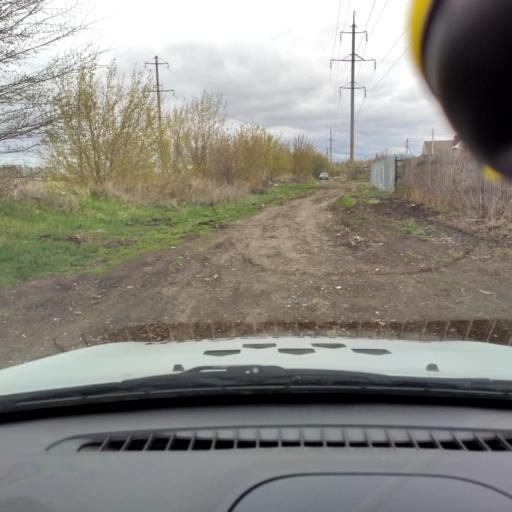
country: RU
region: Samara
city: Tol'yatti
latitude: 53.5871
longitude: 49.3210
